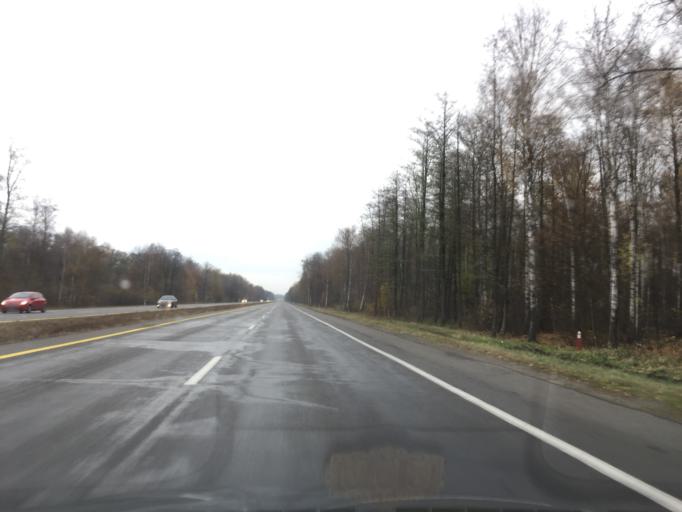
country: BY
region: Gomel
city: Horad Rechytsa
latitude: 52.3493
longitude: 30.5869
